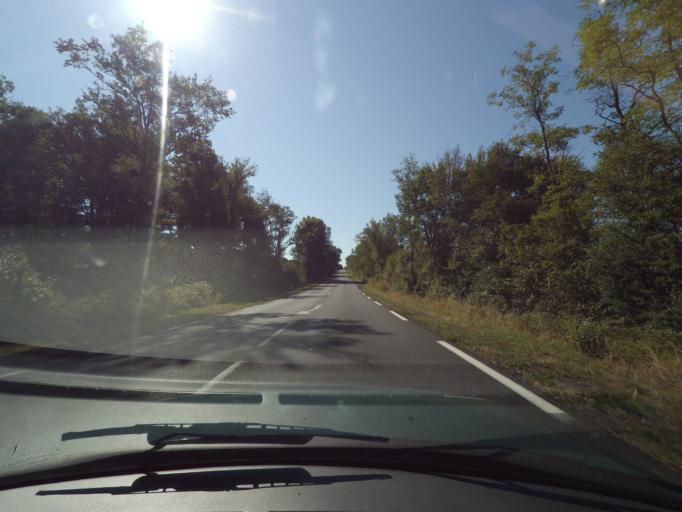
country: FR
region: Poitou-Charentes
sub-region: Departement de la Vienne
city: Lussac-les-Chateaux
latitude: 46.3528
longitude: 0.7852
